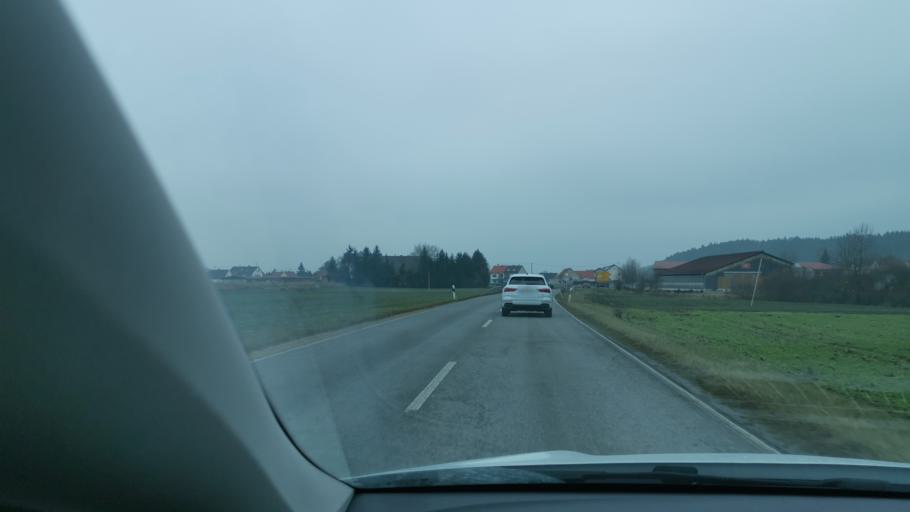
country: DE
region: Bavaria
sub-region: Swabia
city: Todtenweis
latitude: 48.5120
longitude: 10.9175
